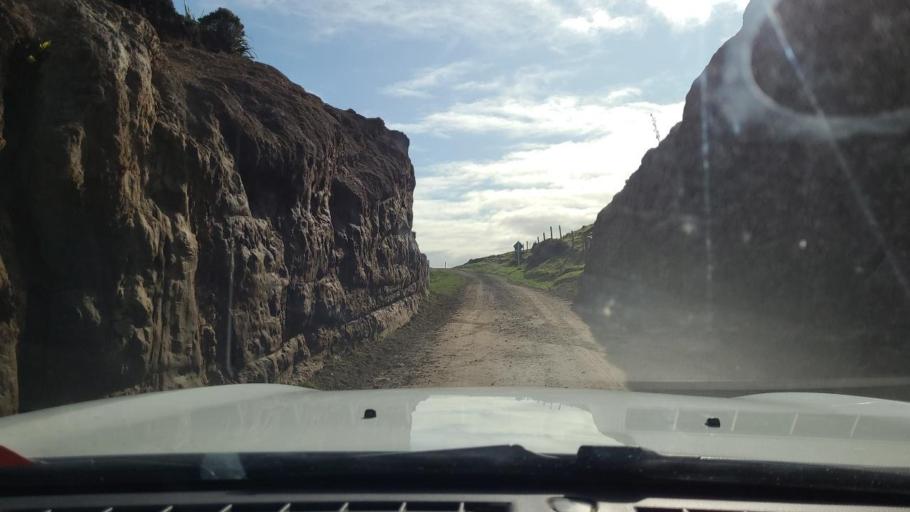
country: NZ
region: Chatham Islands
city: Waitangi
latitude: -44.0396
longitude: -176.6445
